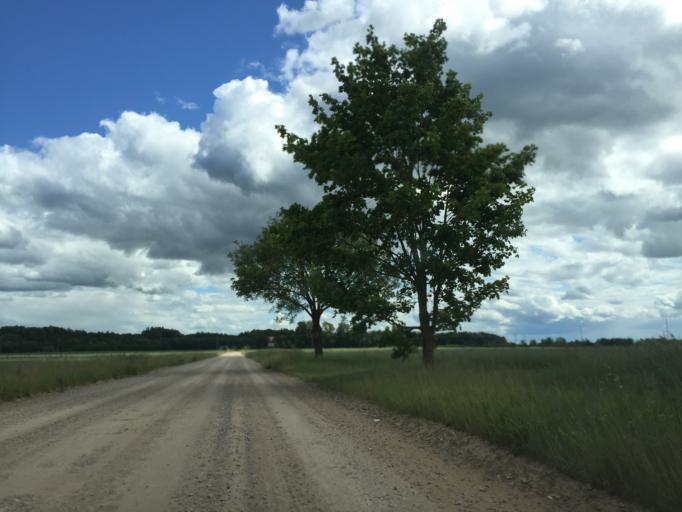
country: LV
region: Lecava
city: Iecava
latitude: 56.5021
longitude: 24.3579
